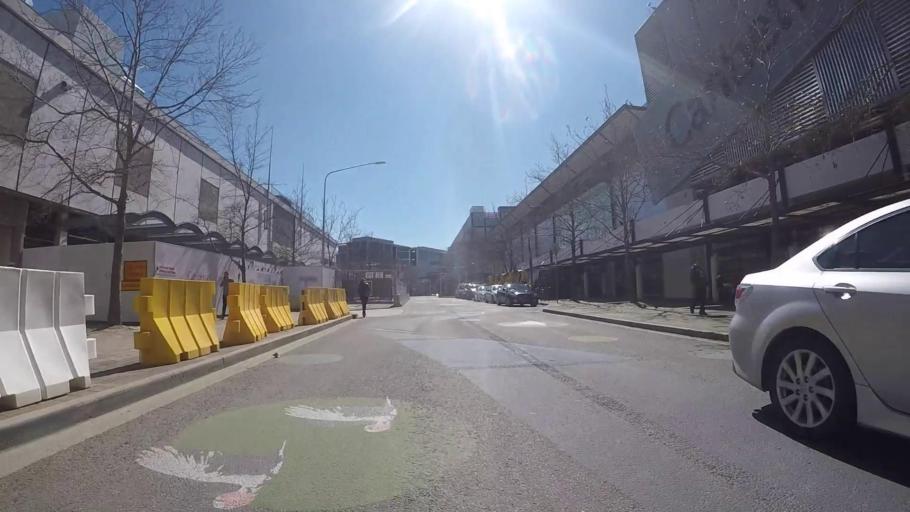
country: AU
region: Australian Capital Territory
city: Canberra
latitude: -35.2799
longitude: 149.1338
